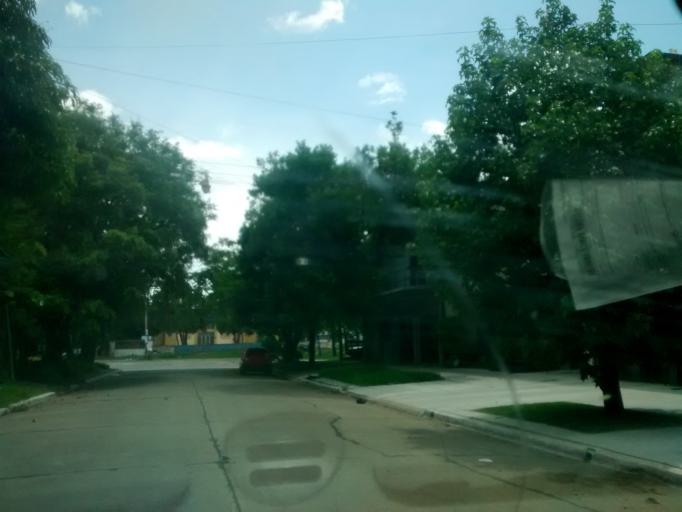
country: AR
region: Chaco
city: Resistencia
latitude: -27.4398
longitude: -58.9861
